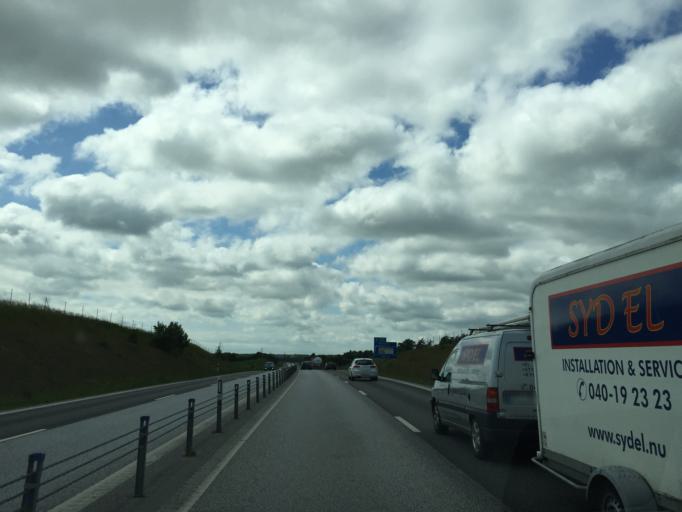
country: SE
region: Skane
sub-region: Trelleborgs Kommun
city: Anderslov
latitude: 55.5030
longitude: 13.3700
